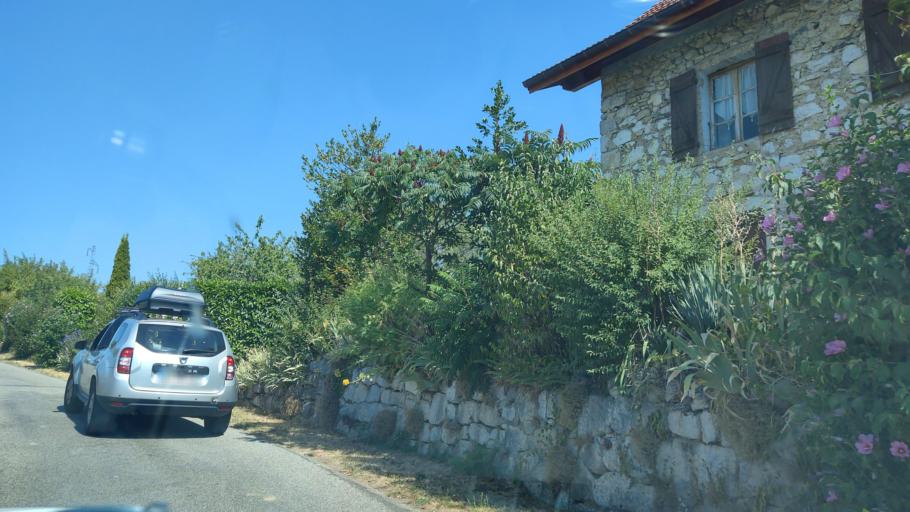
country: FR
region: Rhone-Alpes
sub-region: Departement de la Savoie
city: Novalaise
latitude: 45.5995
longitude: 5.7845
